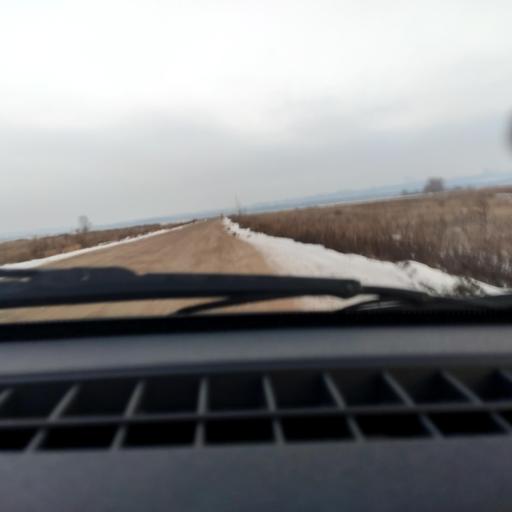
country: RU
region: Bashkortostan
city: Mikhaylovka
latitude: 54.8087
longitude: 55.9581
